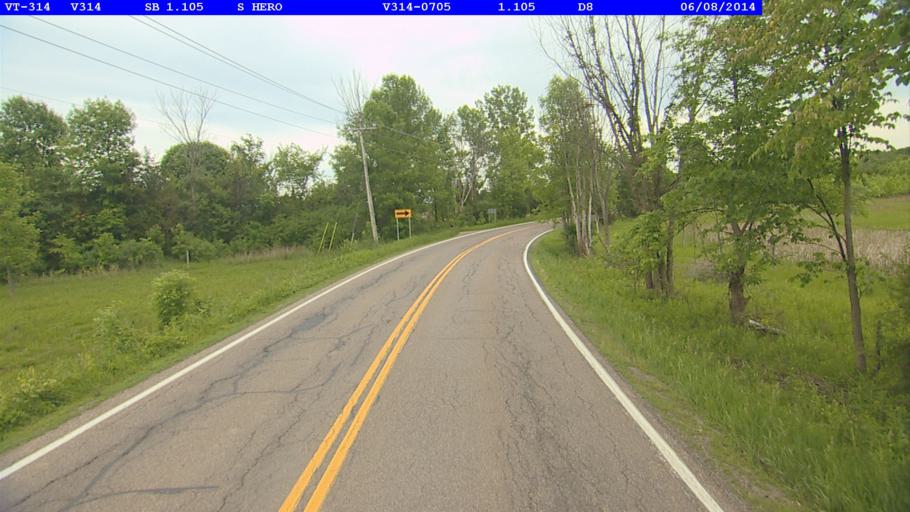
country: US
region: New York
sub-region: Clinton County
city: Cumberland Head
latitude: 44.6738
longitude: -73.3387
